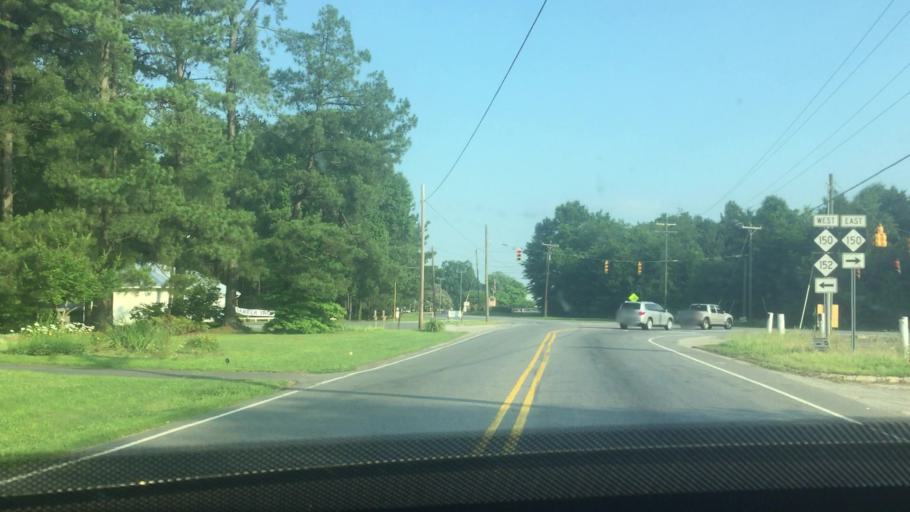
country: US
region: North Carolina
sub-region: Iredell County
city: Mooresville
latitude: 35.5975
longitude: -80.7641
